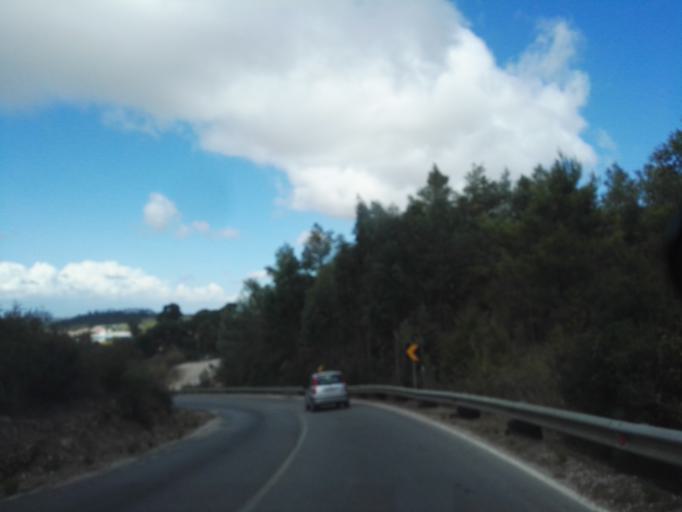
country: PT
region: Setubal
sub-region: Sesimbra
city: Sesimbra
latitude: 38.4630
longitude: -9.0954
